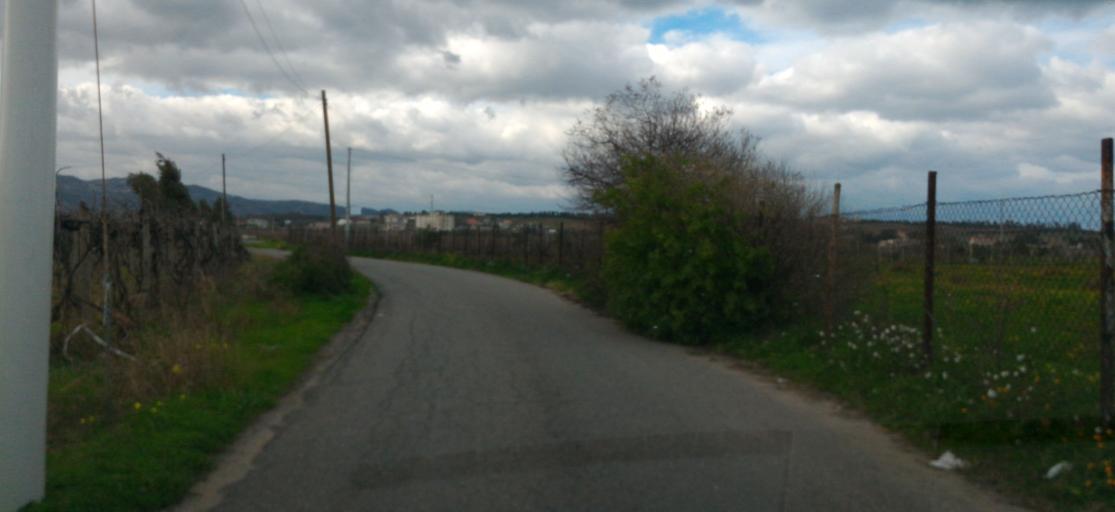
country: IT
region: Calabria
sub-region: Provincia di Crotone
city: Ciro Marina
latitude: 39.3906
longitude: 17.1386
